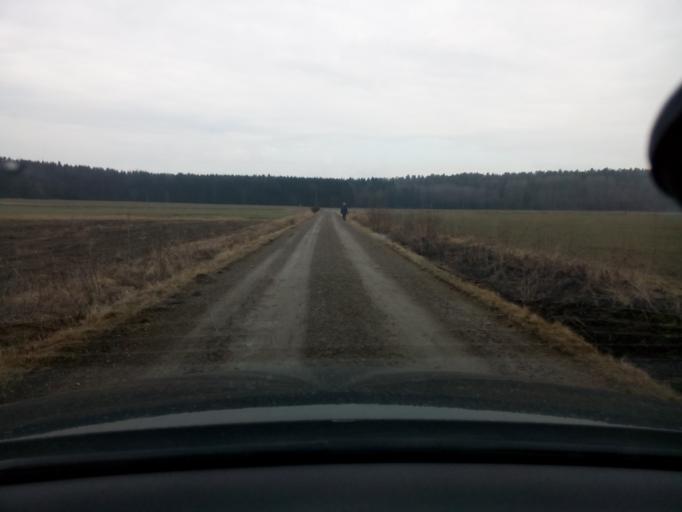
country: SE
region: Soedermanland
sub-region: Trosa Kommun
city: Vagnharad
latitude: 58.9308
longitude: 17.4296
